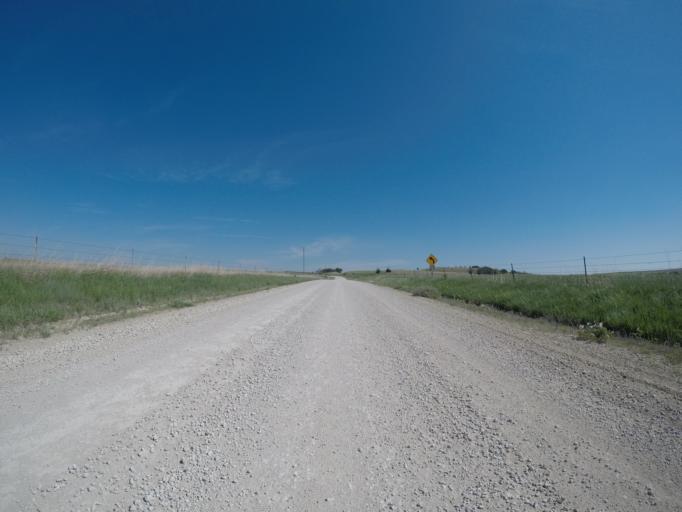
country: US
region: Kansas
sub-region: Wabaunsee County
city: Alma
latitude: 39.0122
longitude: -96.1137
